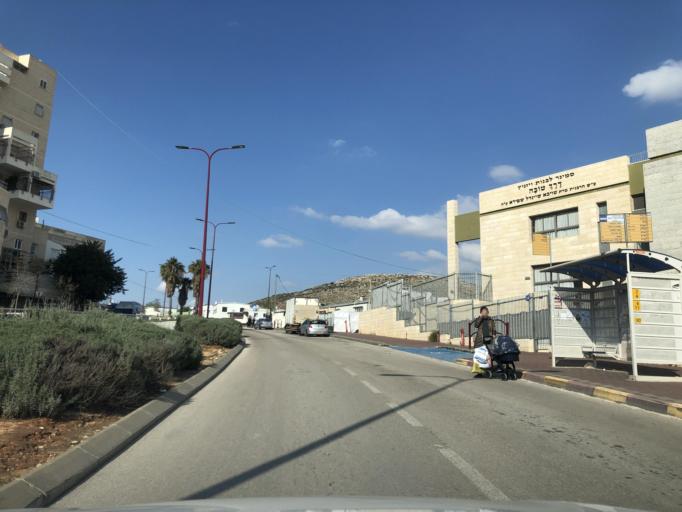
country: IL
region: Jerusalem
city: Modiin Ilit
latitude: 31.9379
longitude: 35.0473
